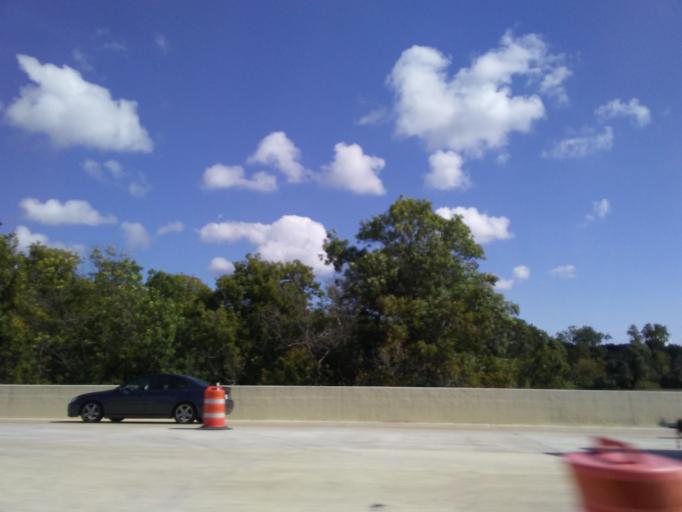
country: US
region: Wisconsin
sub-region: Dane County
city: Shorewood Hills
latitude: 43.0454
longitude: -89.4707
